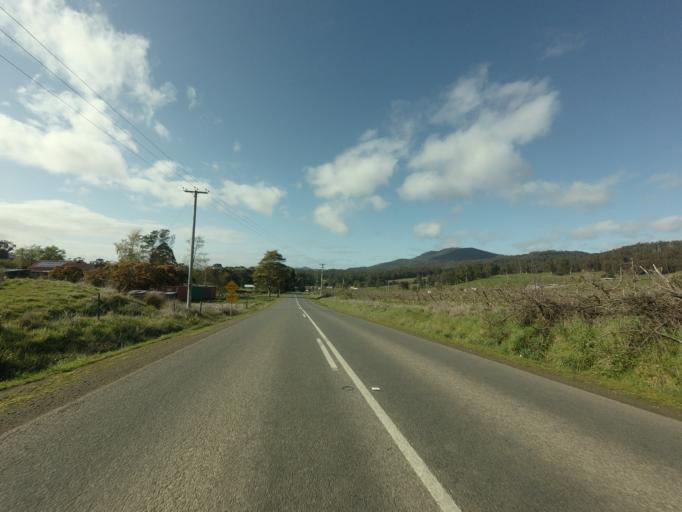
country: AU
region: Tasmania
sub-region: Huon Valley
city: Geeveston
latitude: -43.1859
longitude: 146.9563
